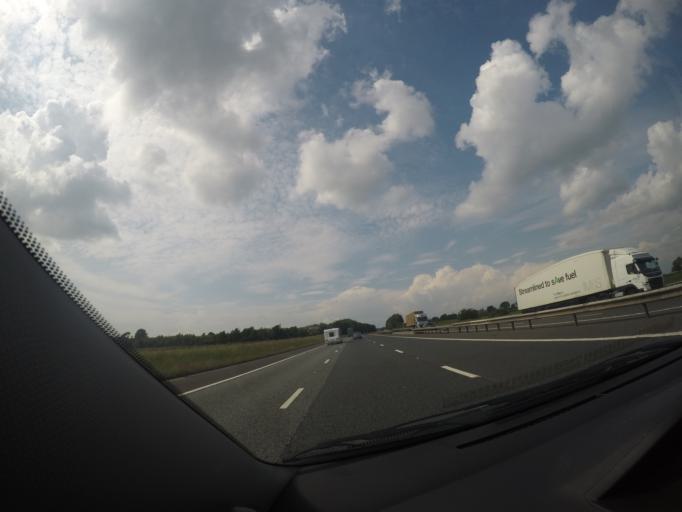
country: GB
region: England
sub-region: Cumbria
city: Scotby
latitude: 54.8119
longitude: -2.8806
